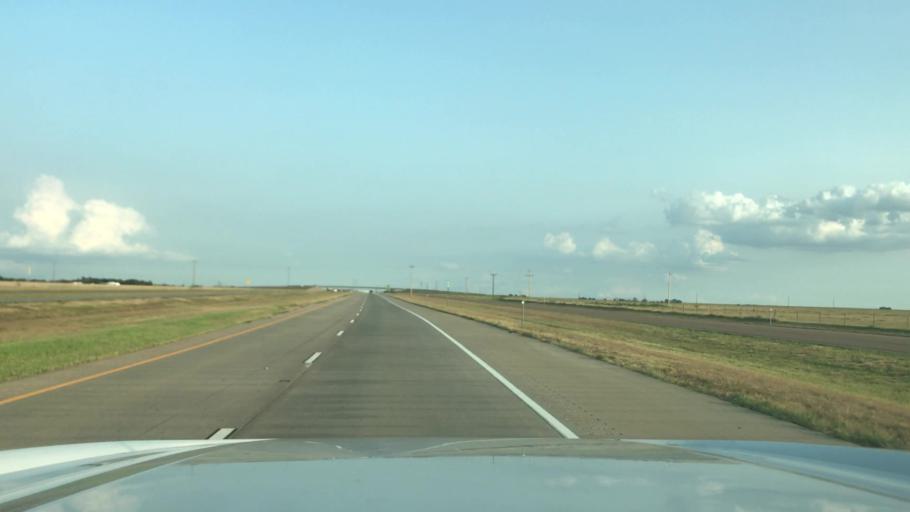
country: US
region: Texas
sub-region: Swisher County
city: Tulia
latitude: 34.3787
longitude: -101.7744
